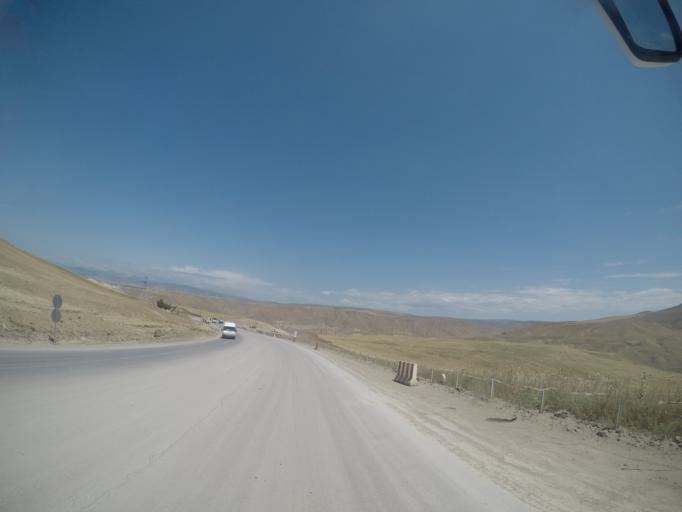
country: AZ
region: Qobustan
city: Qobustan
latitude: 40.5443
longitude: 48.7719
